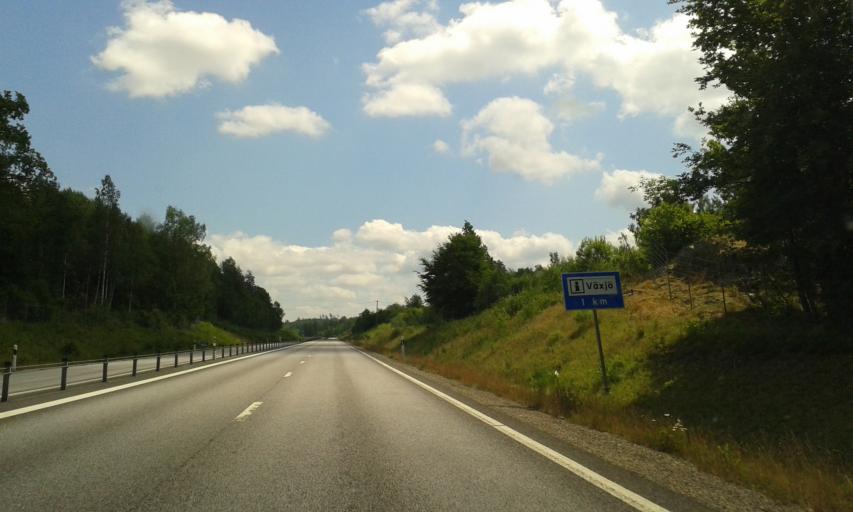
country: SE
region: Kronoberg
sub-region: Vaxjo Kommun
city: Gemla
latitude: 56.9013
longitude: 14.6714
